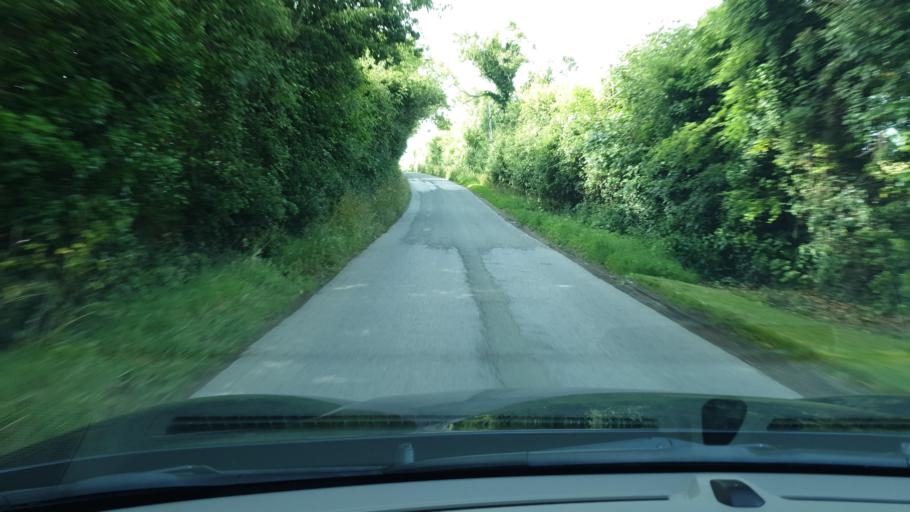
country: IE
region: Leinster
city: Balrothery
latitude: 53.5694
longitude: -6.1646
